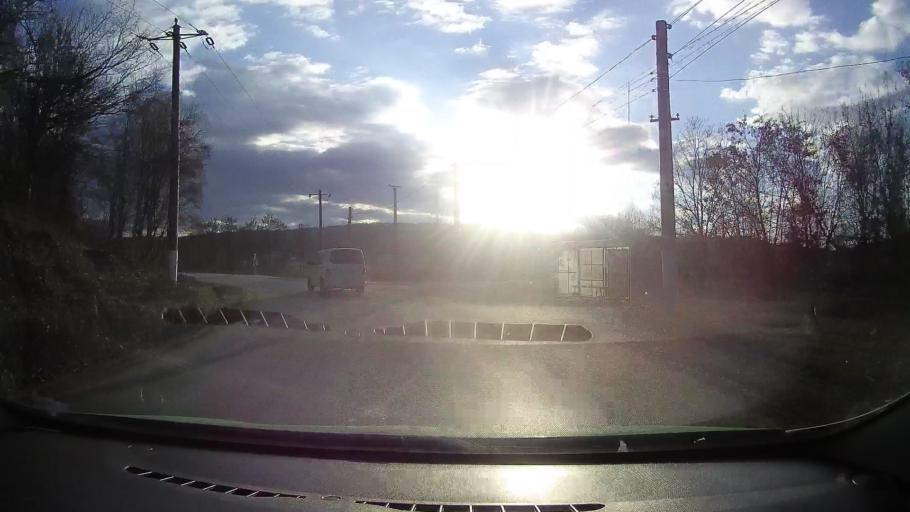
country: RO
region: Dambovita
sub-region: Comuna Ocnita
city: Ocnita
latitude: 44.9696
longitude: 25.5483
